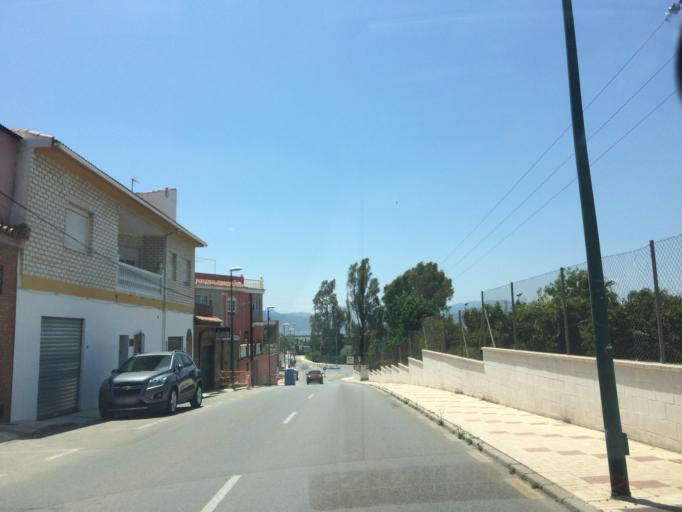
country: ES
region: Andalusia
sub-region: Provincia de Malaga
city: Malaga
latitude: 36.7341
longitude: -4.4829
